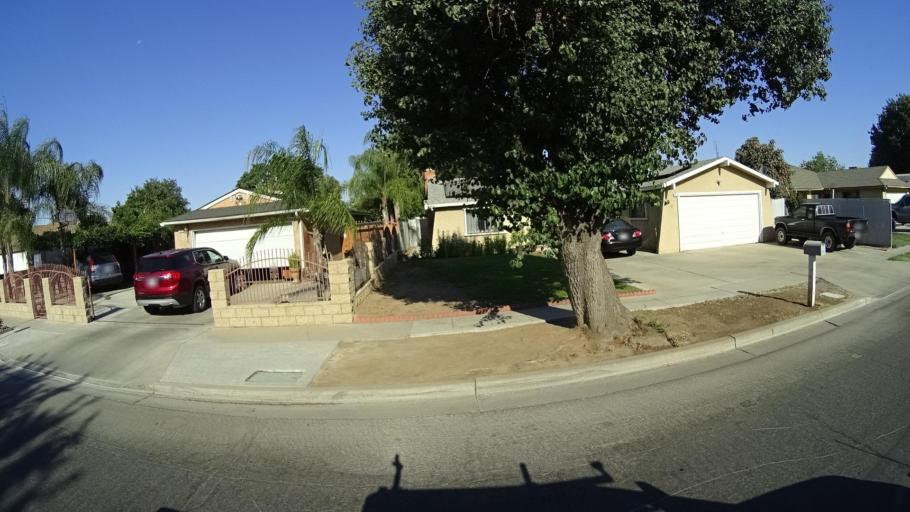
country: US
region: California
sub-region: Fresno County
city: Fresno
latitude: 36.7084
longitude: -119.7483
